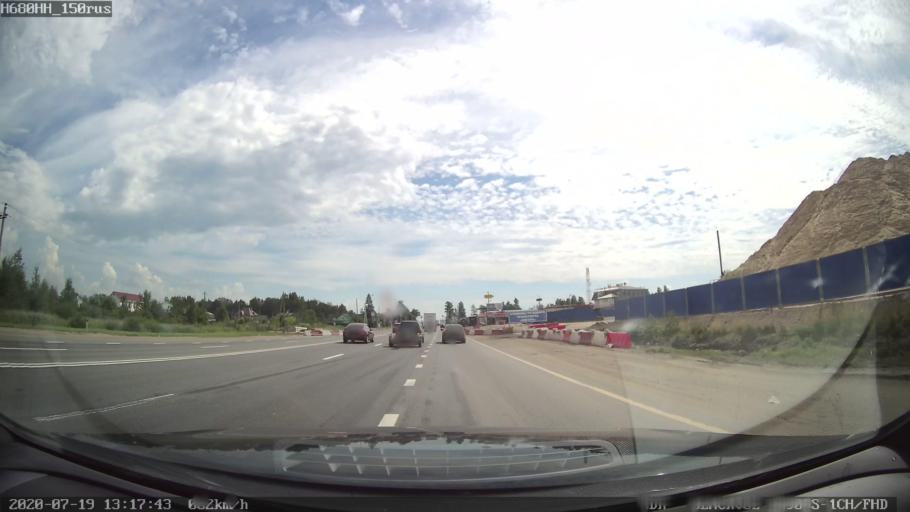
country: RU
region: St.-Petersburg
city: Kolpino
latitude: 59.7064
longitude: 30.5744
